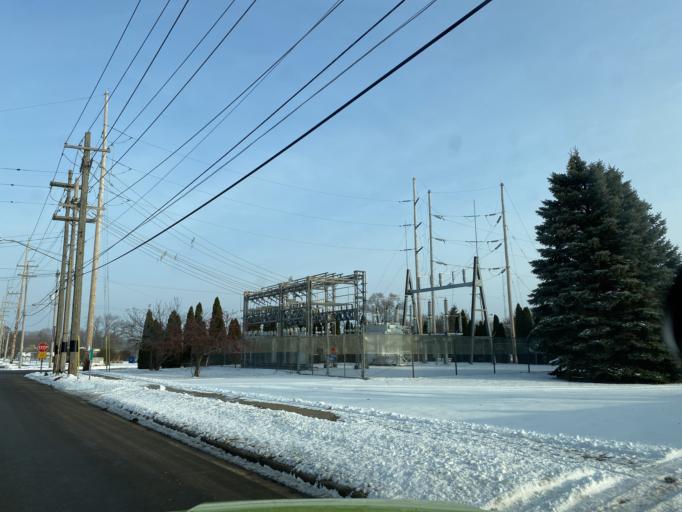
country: US
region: Michigan
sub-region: Ottawa County
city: Hudsonville
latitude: 42.8654
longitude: -85.8651
